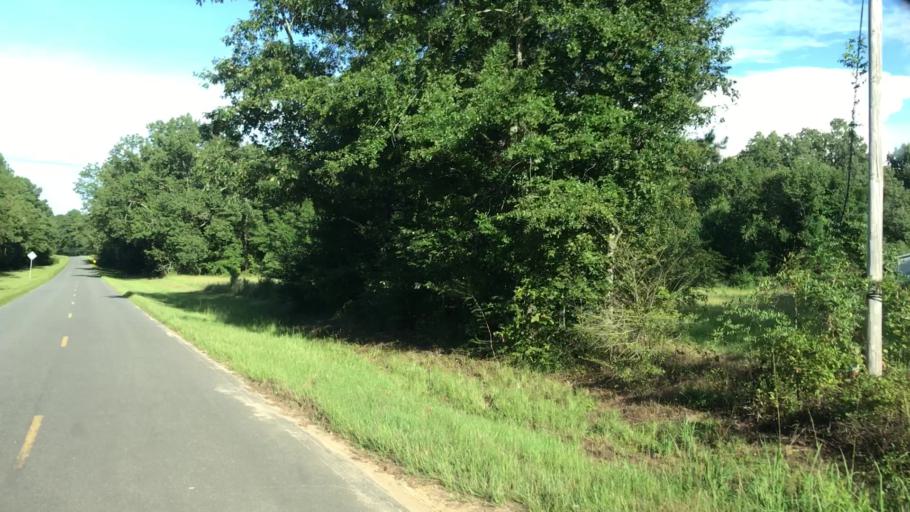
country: US
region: Georgia
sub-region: Jefferson County
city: Wadley
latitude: 32.7996
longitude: -82.3650
